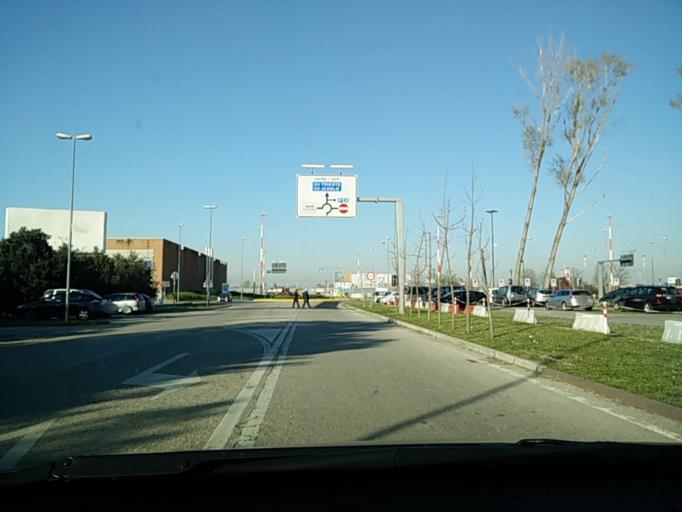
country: IT
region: Veneto
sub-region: Provincia di Venezia
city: Tessera
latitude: 45.5066
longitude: 12.3365
